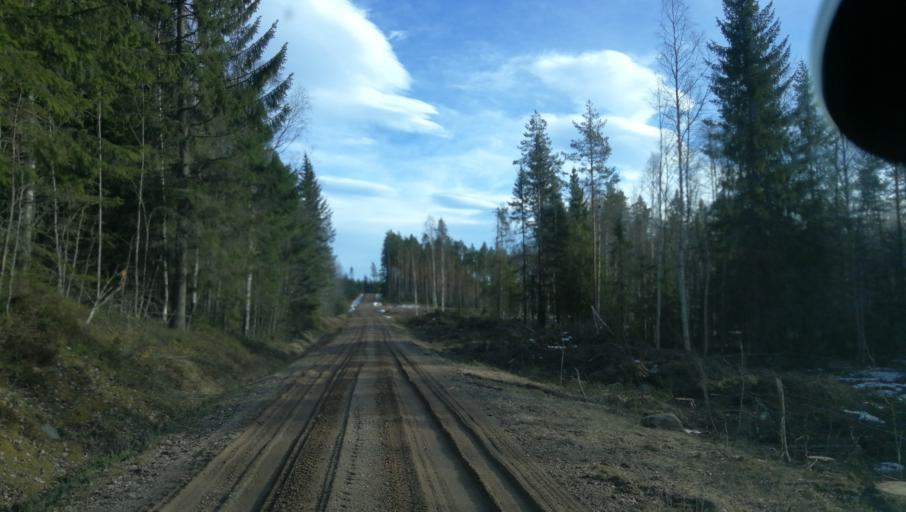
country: SE
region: Dalarna
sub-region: Vansbro Kommun
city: Vansbro
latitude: 60.8134
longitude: 14.2023
